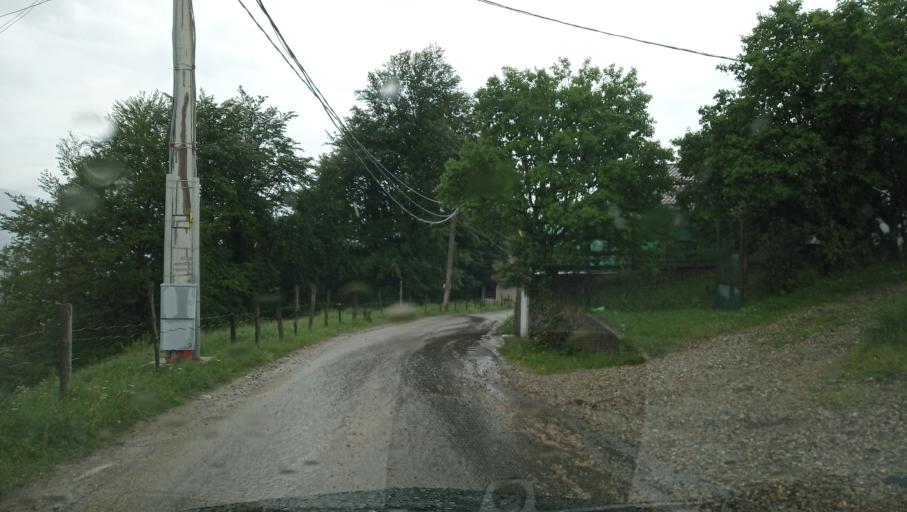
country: RO
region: Hunedoara
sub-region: Oras Petrila
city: Petrila
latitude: 45.3897
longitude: 23.4403
